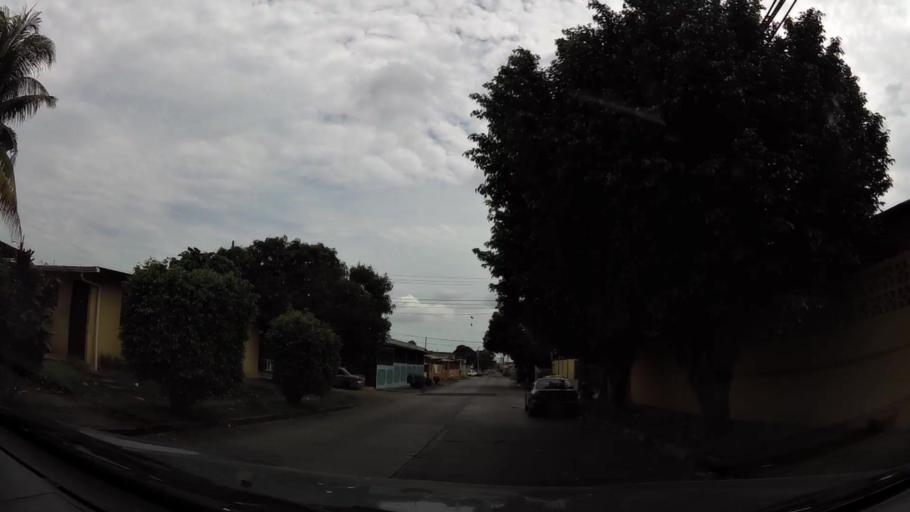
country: PA
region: Panama
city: Tocumen
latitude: 9.0514
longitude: -79.4172
